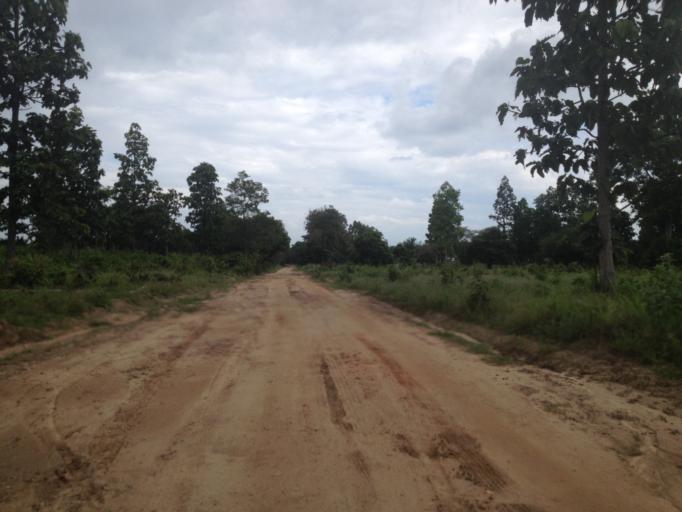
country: TH
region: Chiang Mai
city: Hang Dong
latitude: 18.6922
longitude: 98.8833
